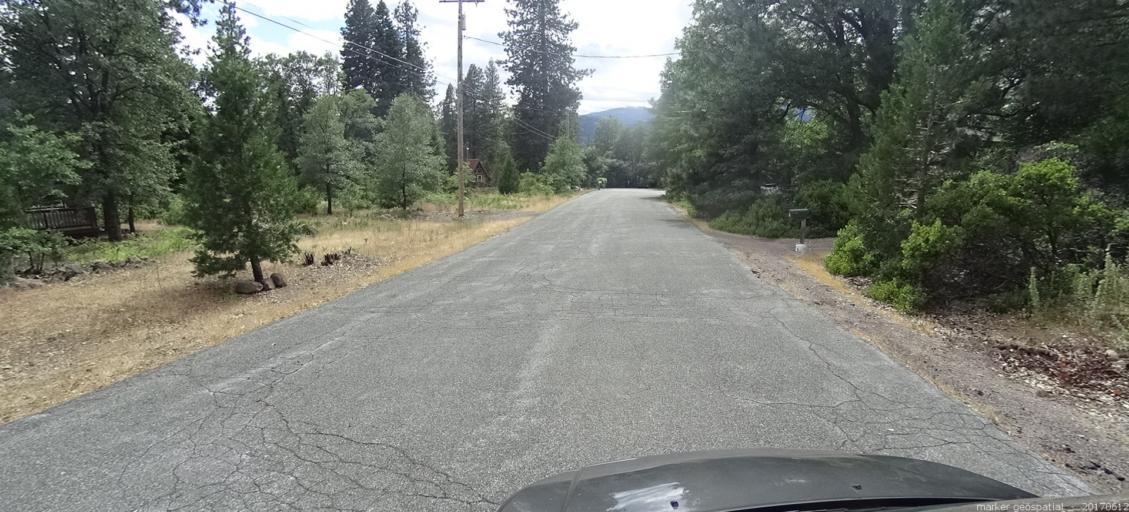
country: US
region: California
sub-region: Siskiyou County
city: Mount Shasta
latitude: 41.3262
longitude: -122.3094
